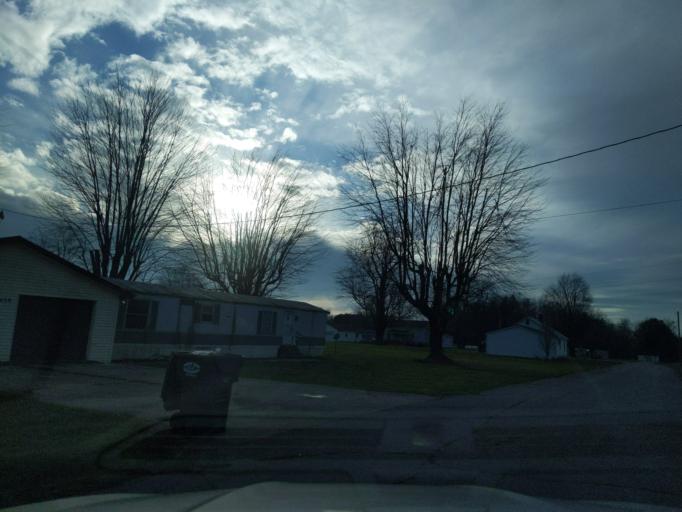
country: US
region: Indiana
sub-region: Decatur County
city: Greensburg
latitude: 39.2124
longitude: -85.4301
